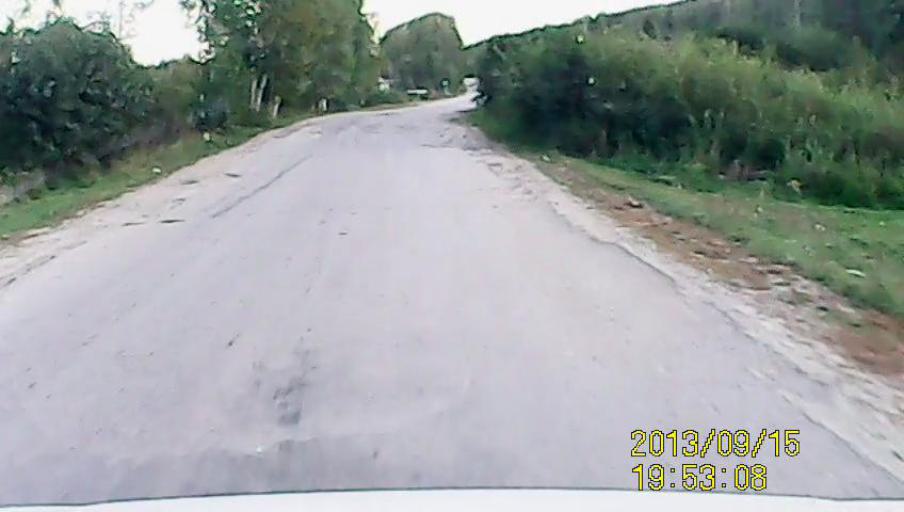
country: RU
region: Chelyabinsk
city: Kyshtym
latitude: 55.7651
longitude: 60.4857
